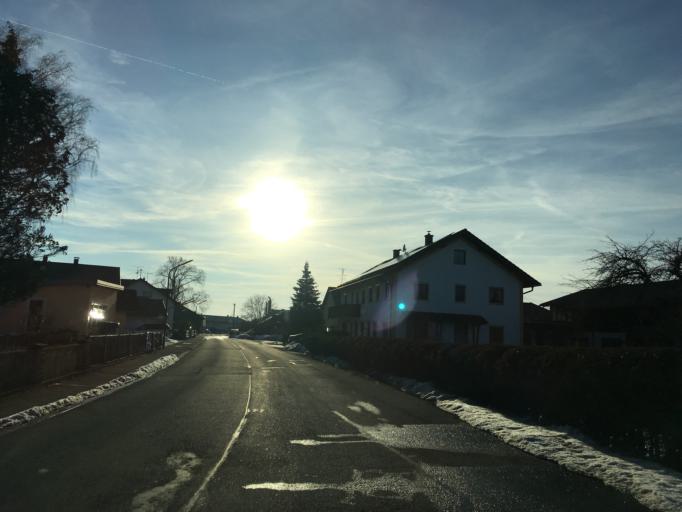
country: DE
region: Bavaria
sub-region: Upper Bavaria
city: Pfaffing
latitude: 48.0835
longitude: 12.0933
